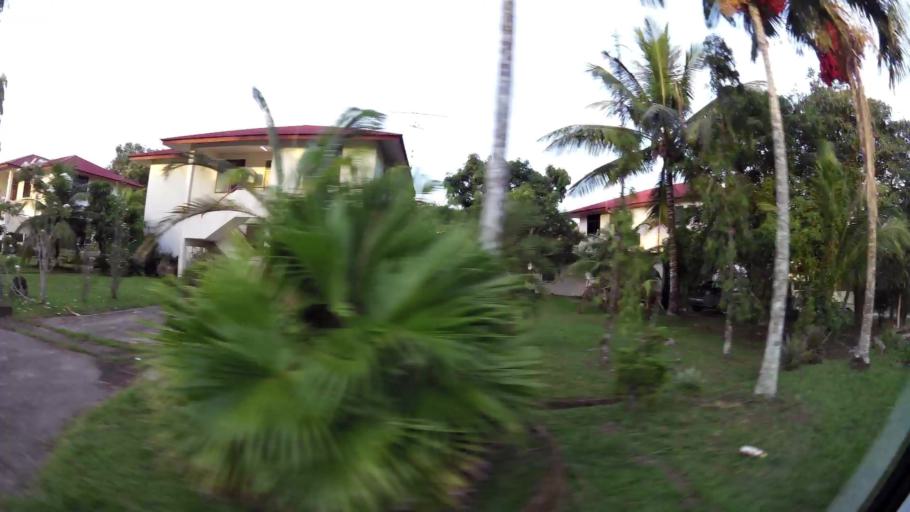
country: BN
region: Brunei and Muara
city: Bandar Seri Begawan
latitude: 4.9308
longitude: 114.8858
